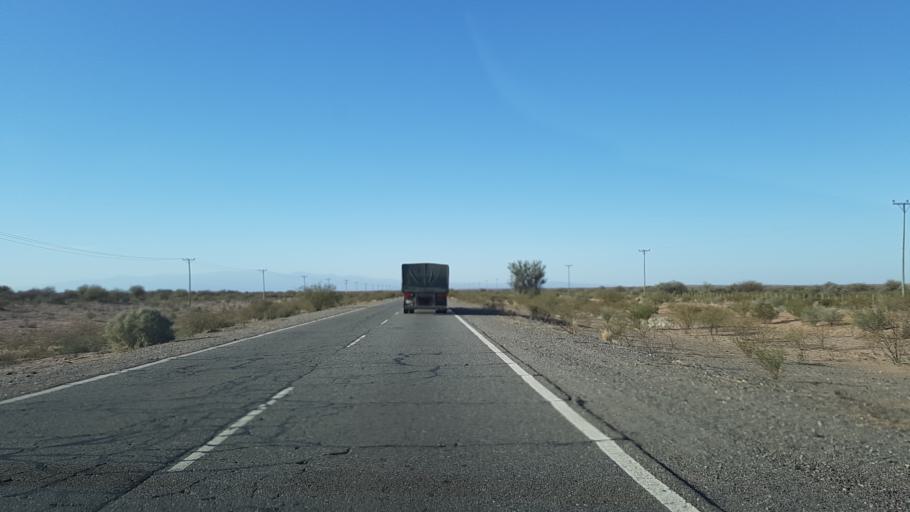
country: AR
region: San Juan
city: Caucete
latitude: -31.6538
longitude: -67.7686
